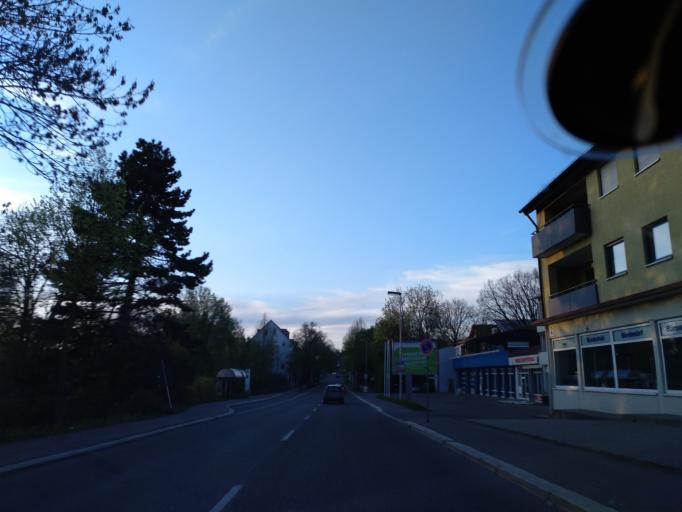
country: DE
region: Baden-Wuerttemberg
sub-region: Regierungsbezirk Stuttgart
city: Crailsheim
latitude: 49.1405
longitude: 10.0735
